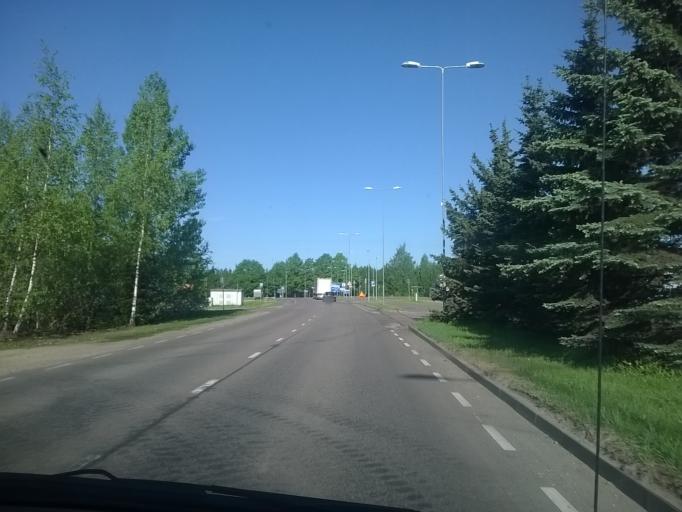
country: EE
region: Valgamaa
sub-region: Valga linn
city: Valga
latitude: 57.7923
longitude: 26.0374
